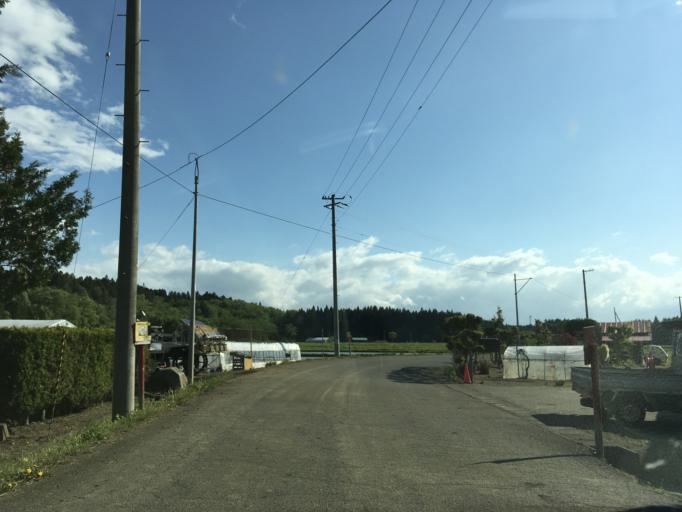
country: JP
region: Iwate
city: Mizusawa
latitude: 39.1639
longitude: 141.0610
